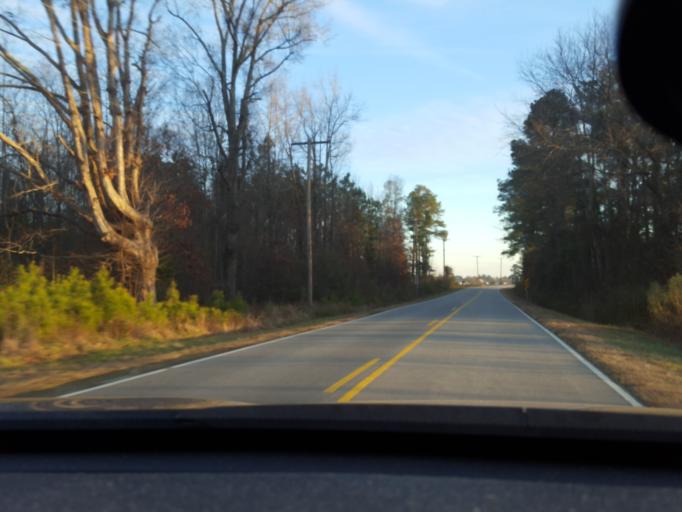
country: US
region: North Carolina
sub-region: Hertford County
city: Ahoskie
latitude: 36.2517
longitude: -77.1222
